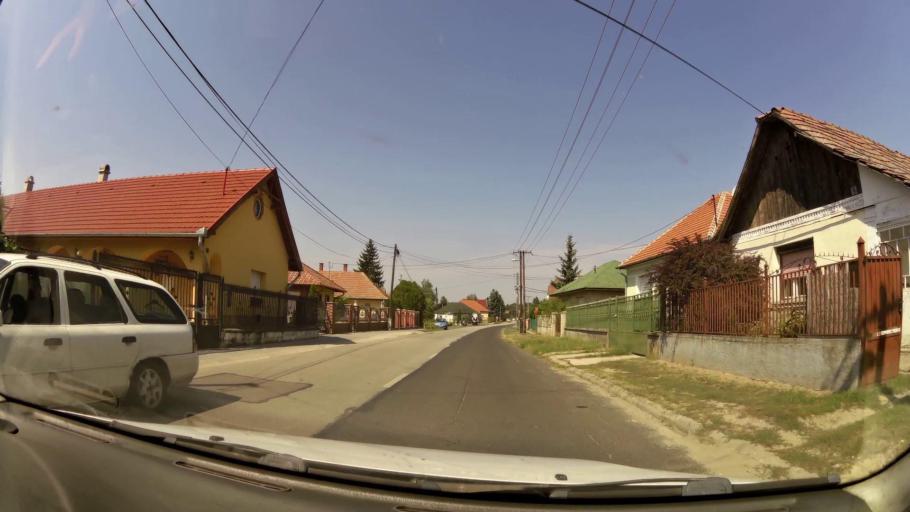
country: HU
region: Pest
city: Tapiosag
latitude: 47.4028
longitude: 19.6240
